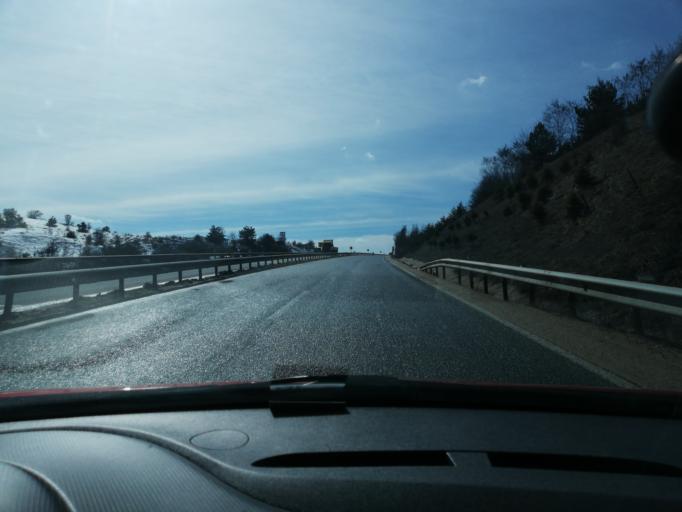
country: TR
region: Karabuk
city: Gozyeri
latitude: 40.8305
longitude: 32.3919
